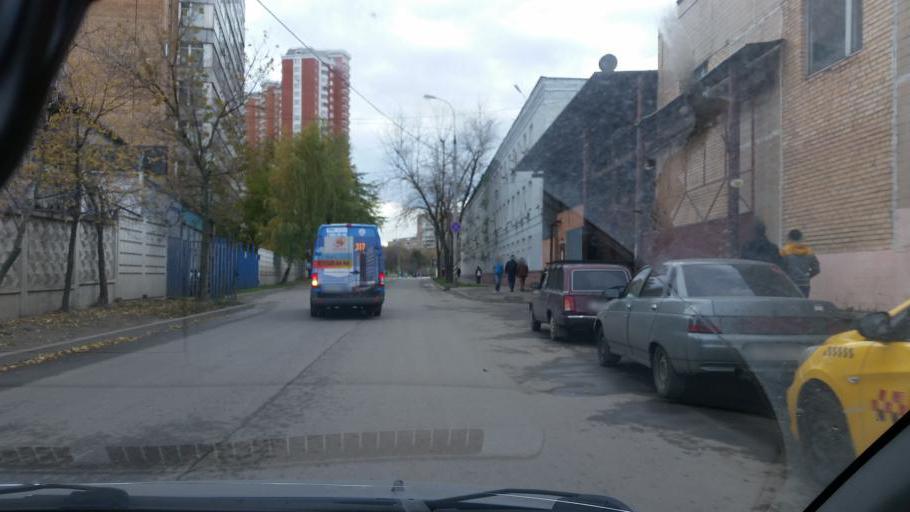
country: RU
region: Moscow
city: Kotlovka
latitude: 55.6749
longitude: 37.6133
